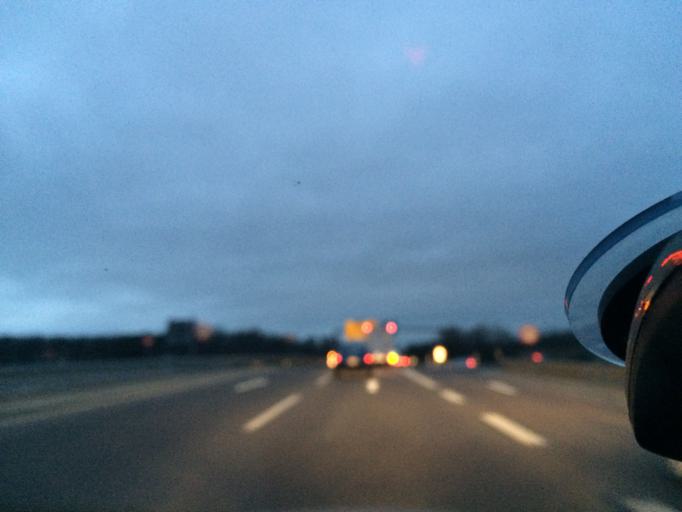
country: DE
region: Hesse
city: Kelsterbach
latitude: 50.0489
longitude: 8.5537
